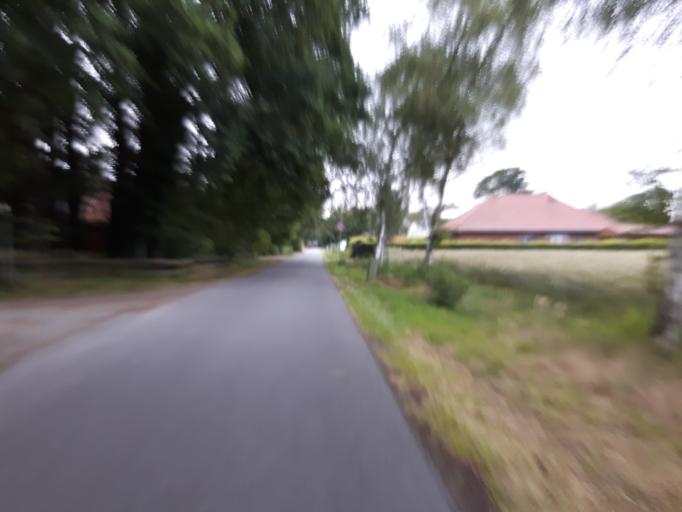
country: DE
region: Lower Saxony
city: Stuhr
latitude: 53.0217
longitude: 8.6973
